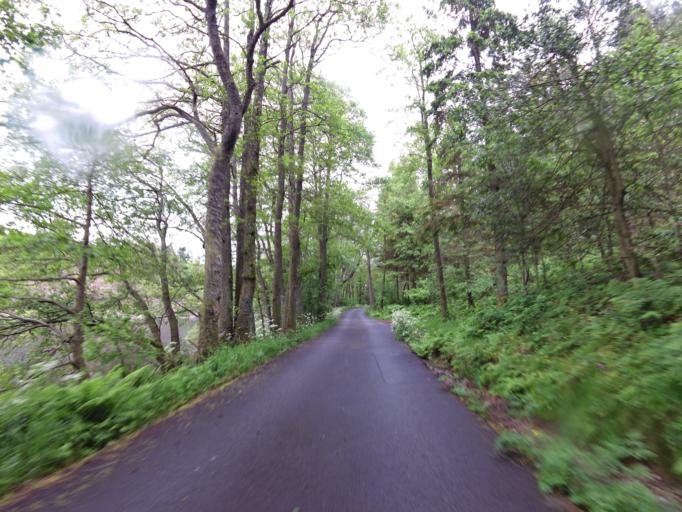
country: NO
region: Vest-Agder
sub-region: Mandal
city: Mandal
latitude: 58.0111
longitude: 7.5174
